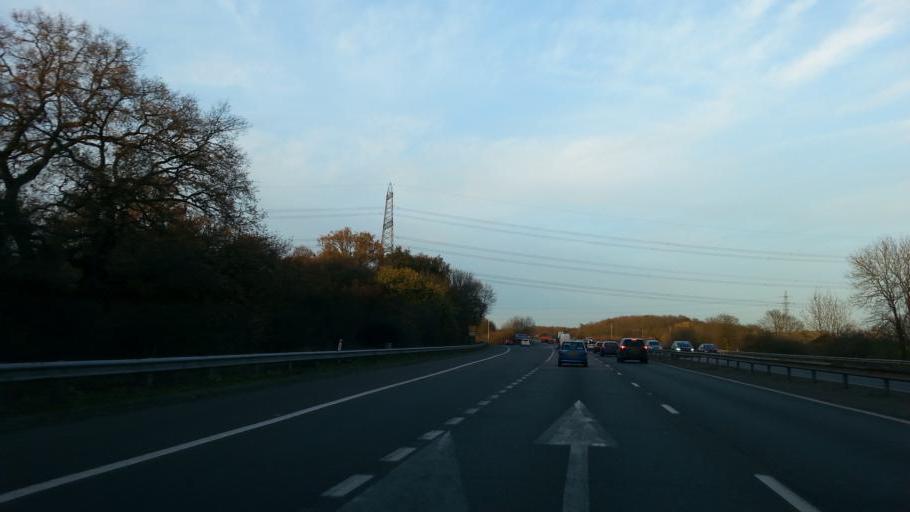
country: GB
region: England
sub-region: Hertfordshire
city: Stevenage
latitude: 51.9245
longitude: -0.2218
